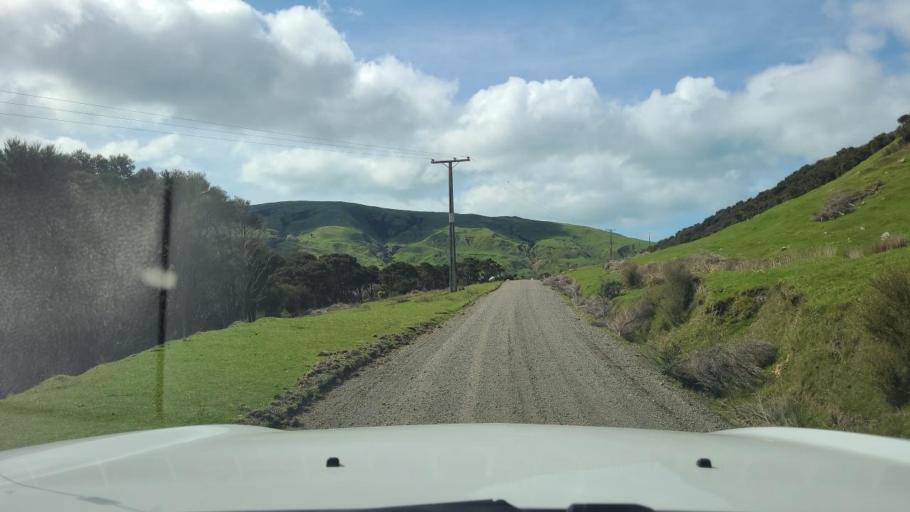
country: NZ
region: Wellington
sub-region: South Wairarapa District
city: Waipawa
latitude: -41.3743
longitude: 175.7179
